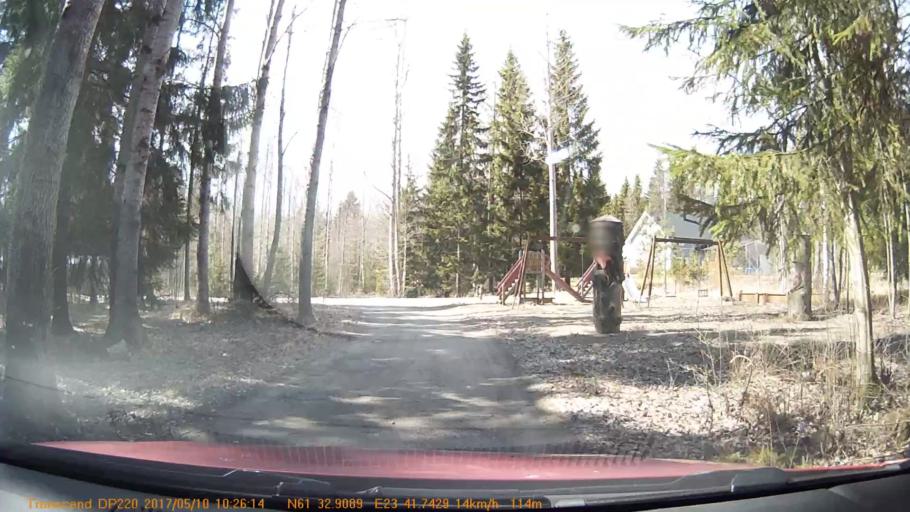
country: FI
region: Pirkanmaa
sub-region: Tampere
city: Yloejaervi
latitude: 61.5485
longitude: 23.6958
